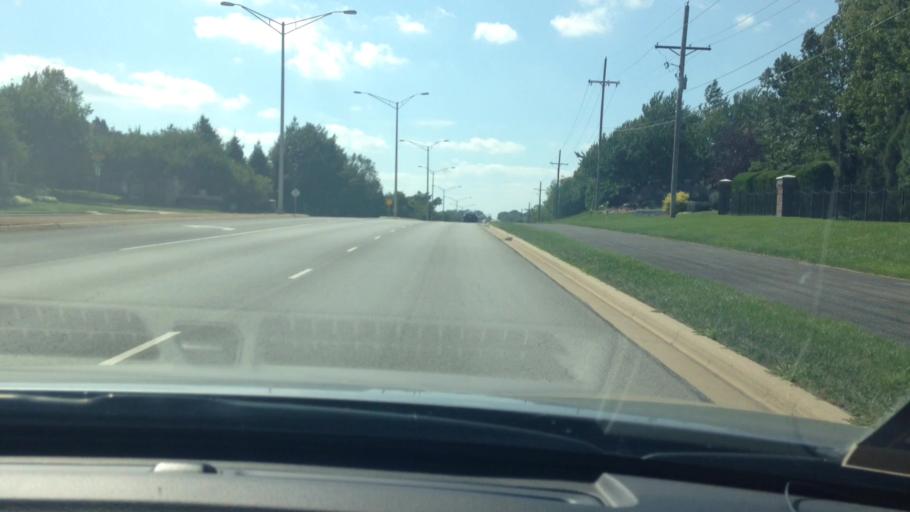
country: US
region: Kansas
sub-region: Johnson County
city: Lenexa
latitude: 38.8692
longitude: -94.6888
